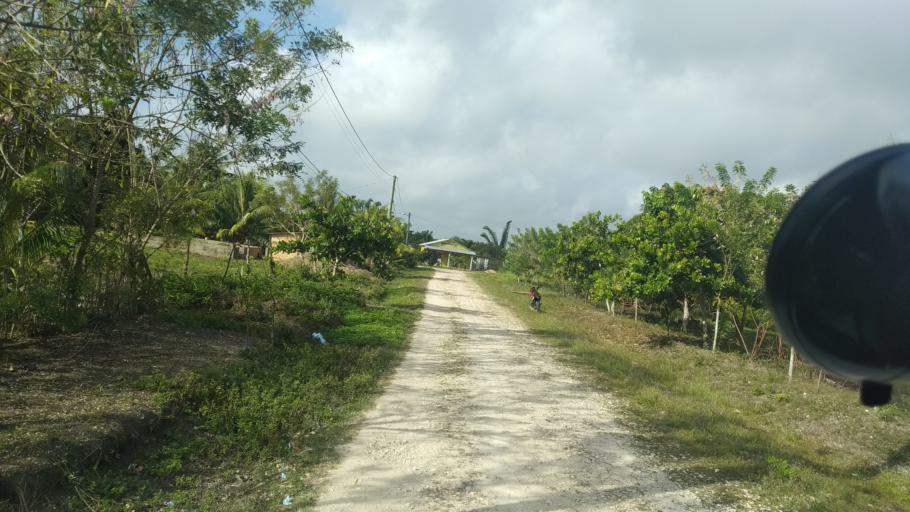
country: BZ
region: Stann Creek
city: Placencia
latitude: 16.5068
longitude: -88.5472
